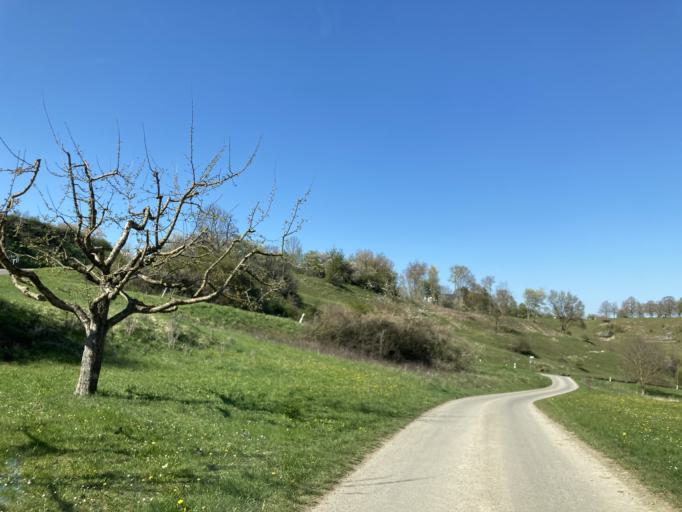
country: DE
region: Baden-Wuerttemberg
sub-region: Tuebingen Region
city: Rottenburg
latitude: 48.5398
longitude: 8.9127
